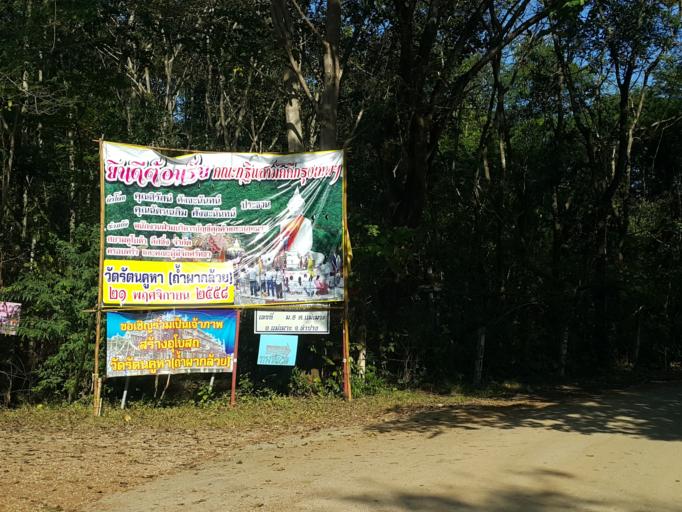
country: TH
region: Lampang
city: Mae Mo
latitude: 18.2926
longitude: 99.6586
